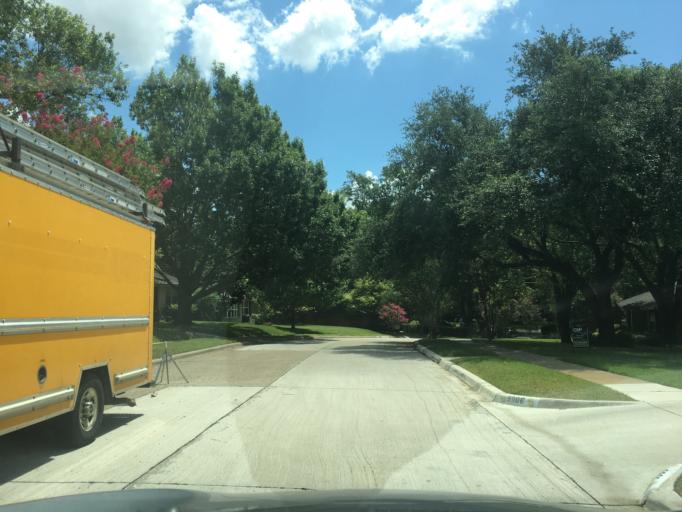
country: US
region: Texas
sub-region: Dallas County
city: Richardson
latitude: 32.8696
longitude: -96.7153
